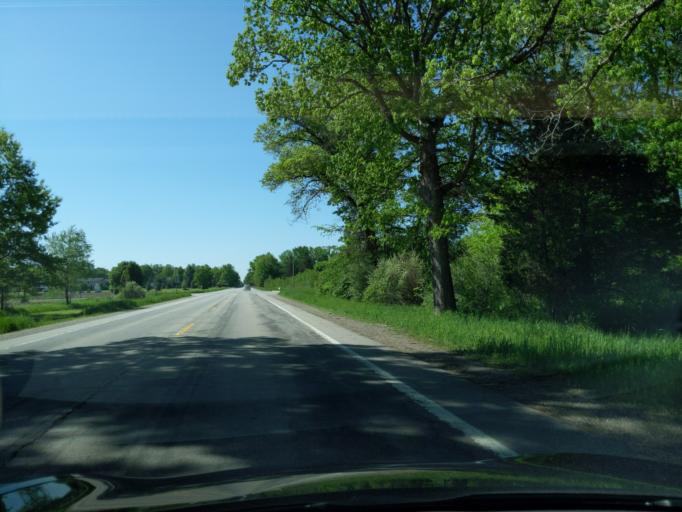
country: US
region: Michigan
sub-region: Ingham County
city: Stockbridge
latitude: 42.4907
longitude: -84.1901
